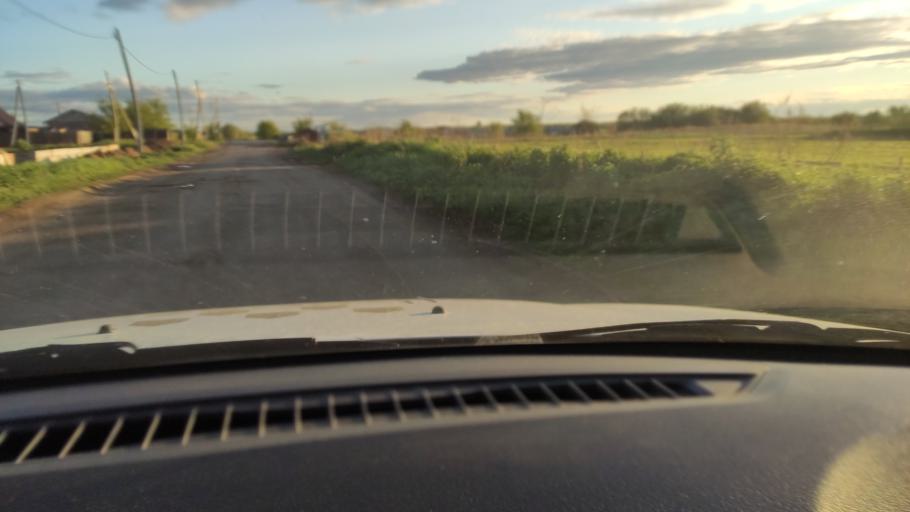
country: RU
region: Perm
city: Kondratovo
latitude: 57.9898
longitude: 56.0993
